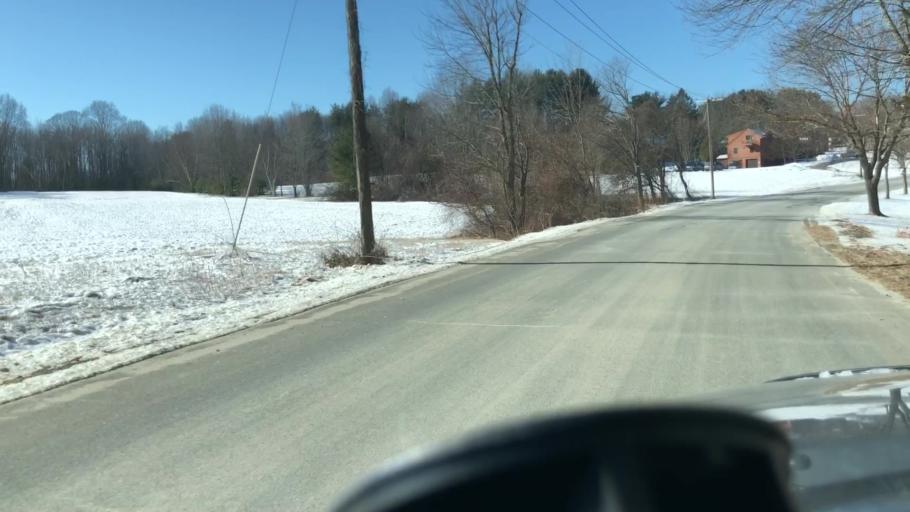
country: US
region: Massachusetts
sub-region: Hampshire County
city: Southampton
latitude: 42.2246
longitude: -72.7282
